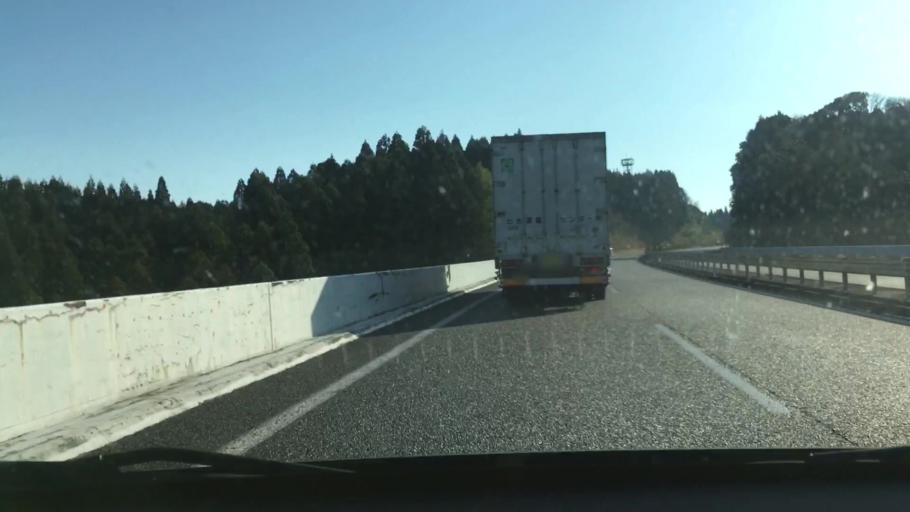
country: JP
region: Kagoshima
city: Kajiki
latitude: 31.9019
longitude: 130.7075
